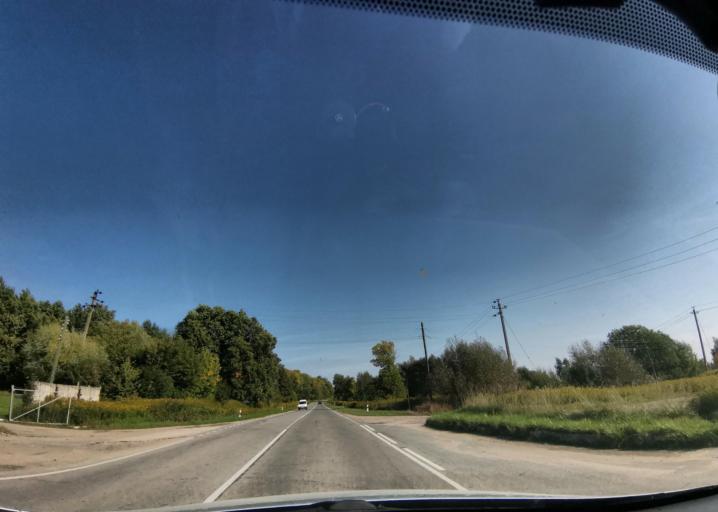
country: RU
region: Kaliningrad
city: Neman
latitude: 55.0183
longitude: 22.1007
